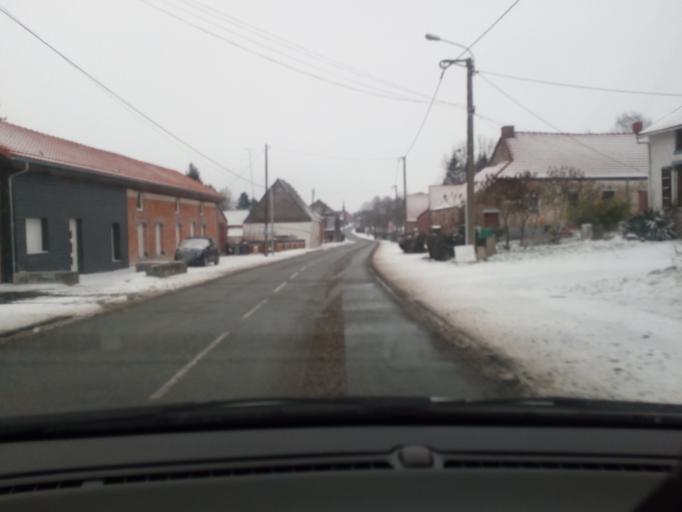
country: FR
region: Nord-Pas-de-Calais
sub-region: Departement du Nord
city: La Longueville
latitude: 50.3212
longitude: 3.8665
